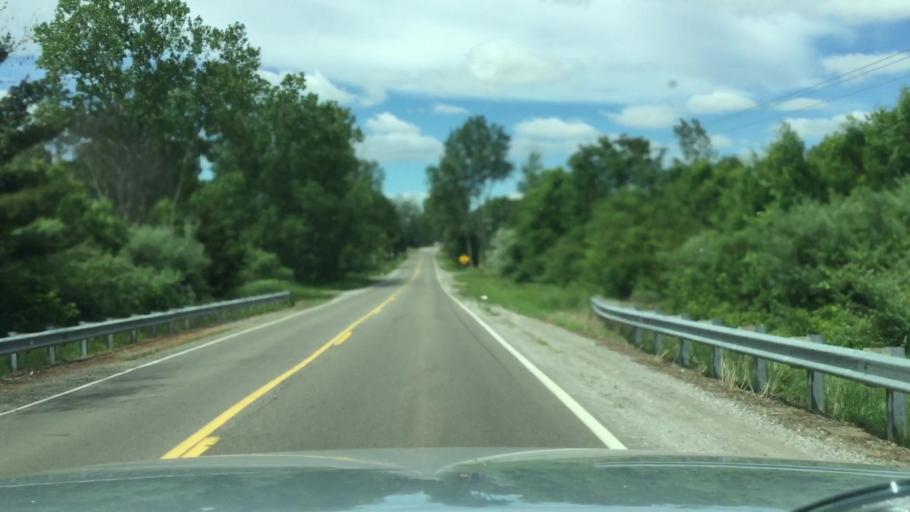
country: US
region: Michigan
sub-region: Genesee County
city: Clio
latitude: 43.1918
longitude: -83.7704
